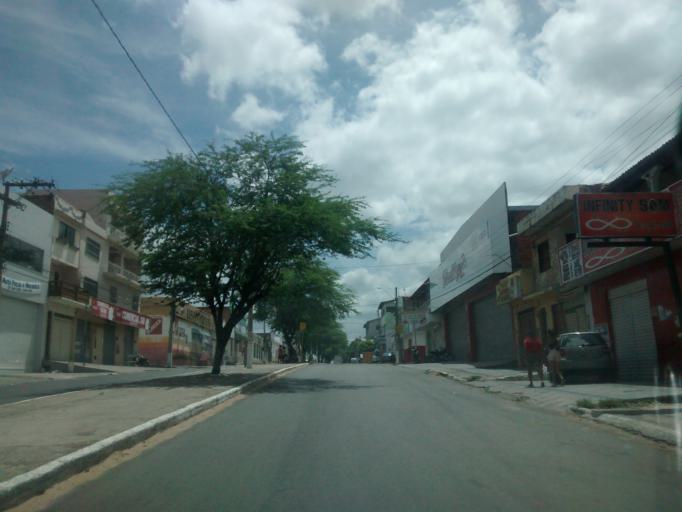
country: BR
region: Bahia
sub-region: Brumado
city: Brumado
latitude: -14.2128
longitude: -41.6753
